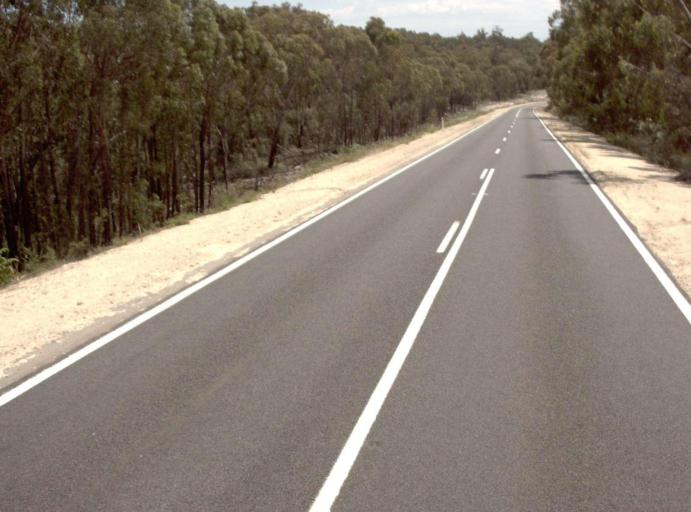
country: AU
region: New South Wales
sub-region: Bombala
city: Bombala
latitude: -37.5650
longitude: 149.2365
